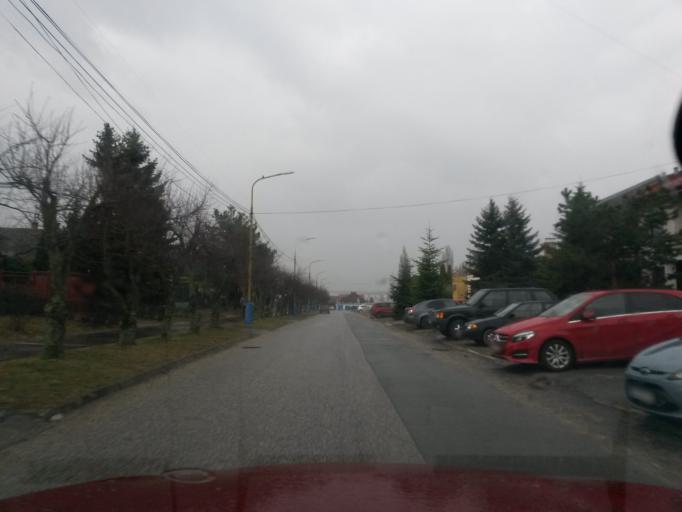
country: SK
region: Kosicky
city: Kosice
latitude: 48.7369
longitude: 21.2914
